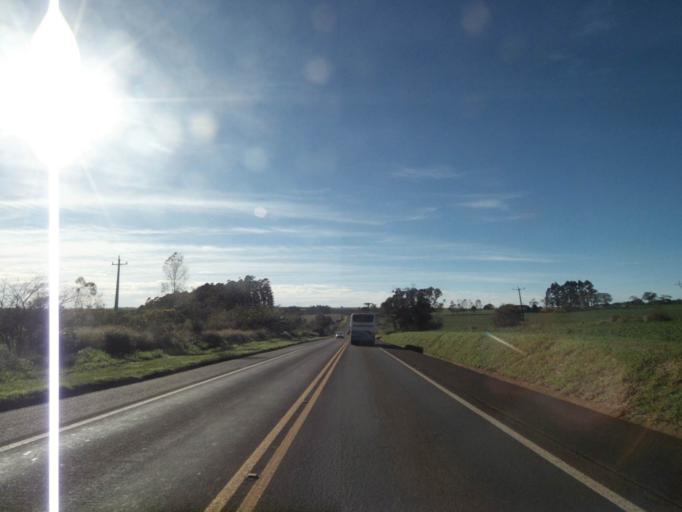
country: BR
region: Parana
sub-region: Cascavel
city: Cascavel
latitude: -25.0290
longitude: -53.5689
